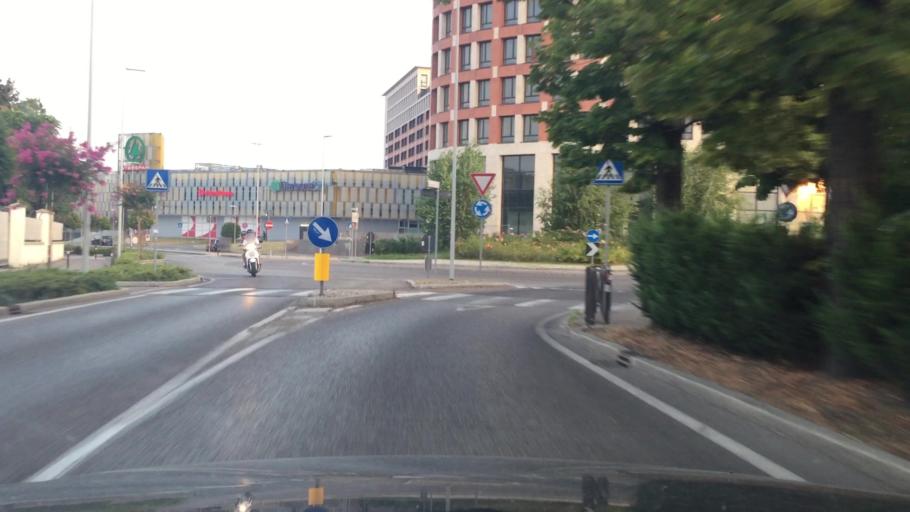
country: IT
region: Emilia-Romagna
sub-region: Provincia di Ferrara
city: Ferrara
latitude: 44.8387
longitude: 11.6015
